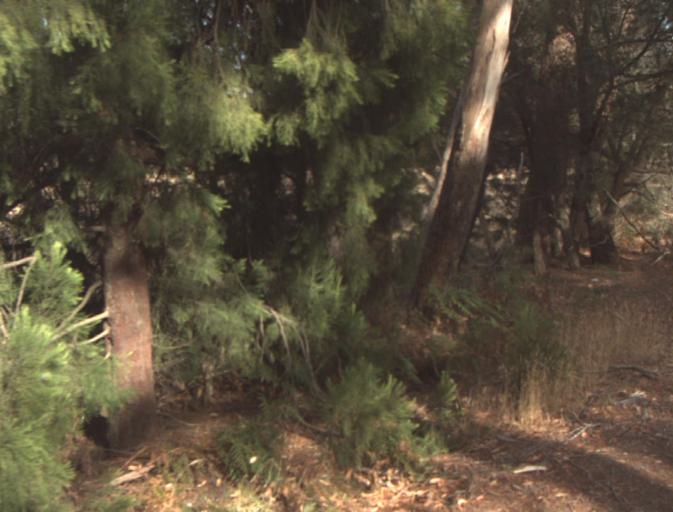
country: AU
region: Tasmania
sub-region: Dorset
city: Bridport
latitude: -41.1218
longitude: 147.2059
